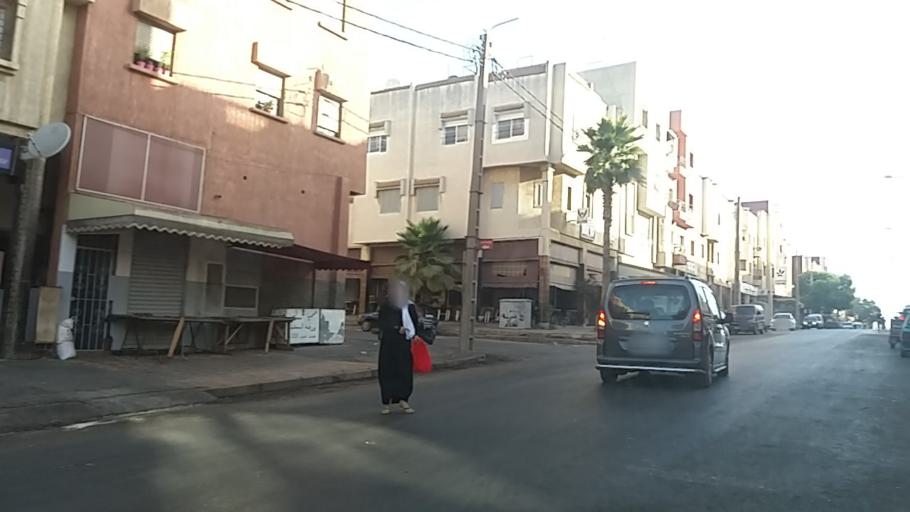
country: MA
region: Gharb-Chrarda-Beni Hssen
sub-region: Kenitra Province
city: Kenitra
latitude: 34.2561
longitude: -6.6226
